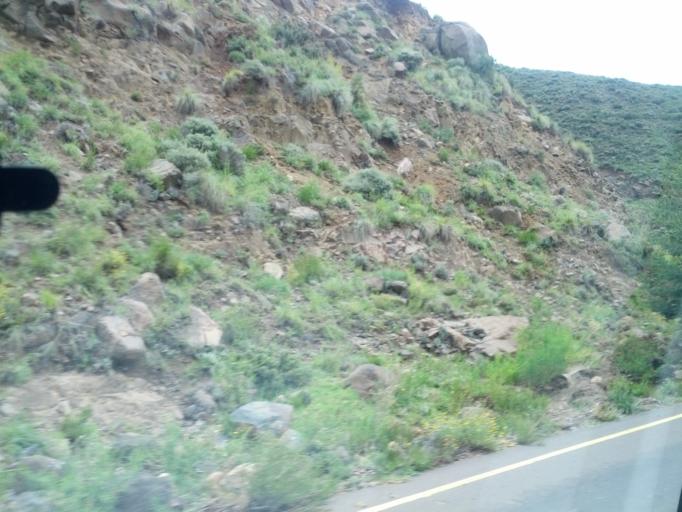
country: LS
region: Butha-Buthe
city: Butha-Buthe
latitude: -29.0543
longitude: 28.3470
